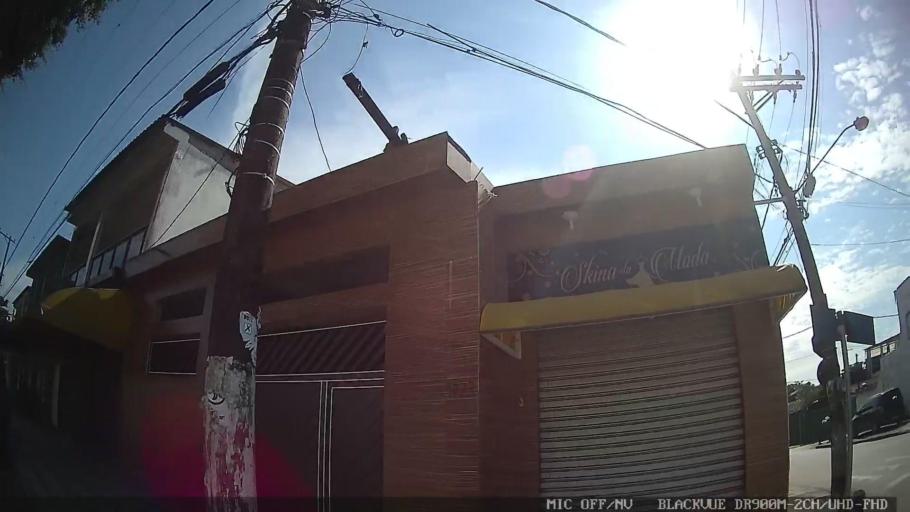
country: BR
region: Sao Paulo
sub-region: Santos
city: Santos
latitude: -23.9485
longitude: -46.2847
